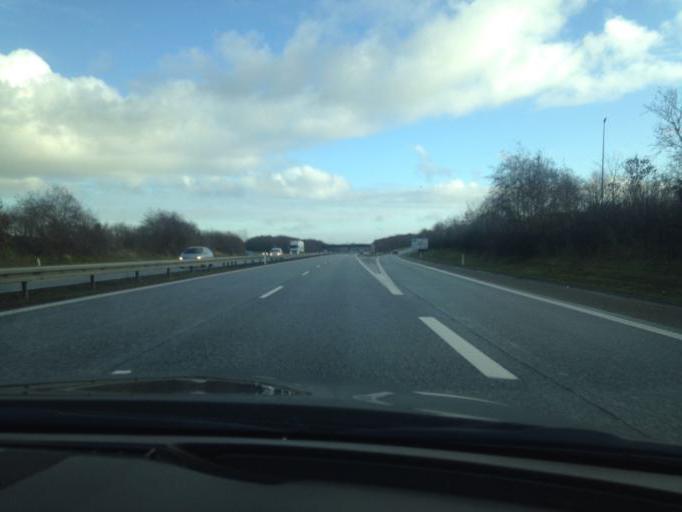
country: DK
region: South Denmark
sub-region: Vejen Kommune
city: Vejen
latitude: 55.4950
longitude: 9.1225
